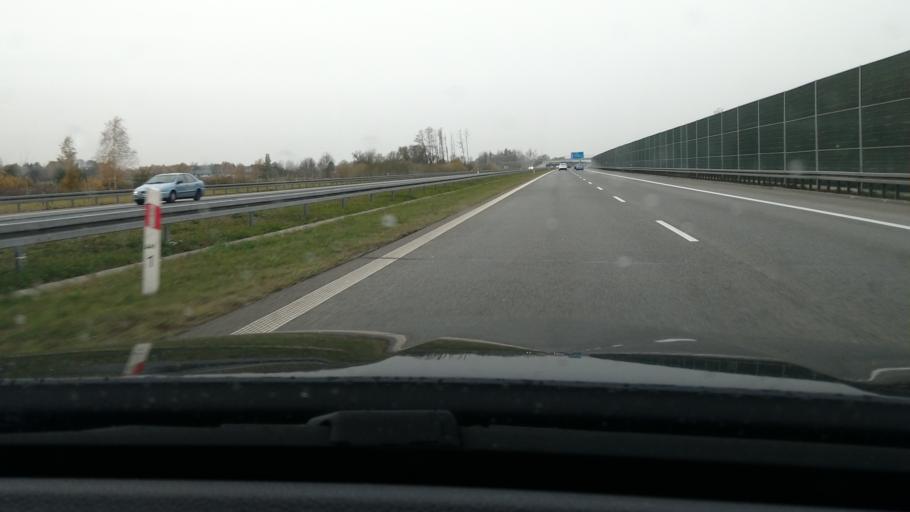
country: PL
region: Masovian Voivodeship
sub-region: Powiat grodziski
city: Milanowek
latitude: 52.1505
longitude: 20.6539
